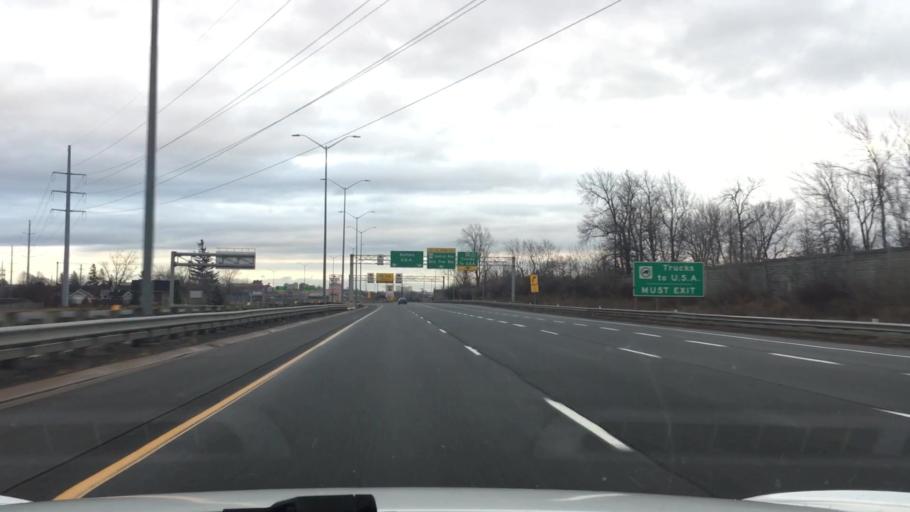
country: CA
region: Ontario
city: Fort Erie
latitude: 42.9092
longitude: -78.9255
